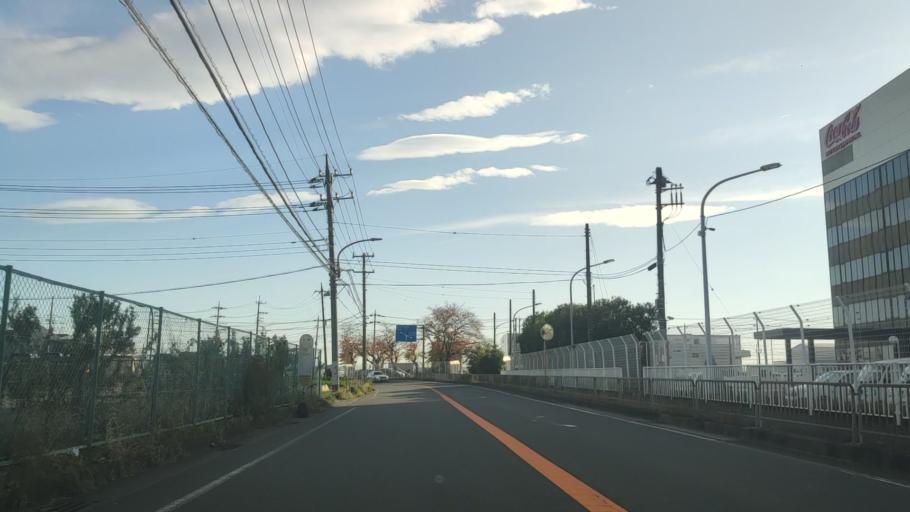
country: JP
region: Kanagawa
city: Atsugi
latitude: 35.4228
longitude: 139.3876
